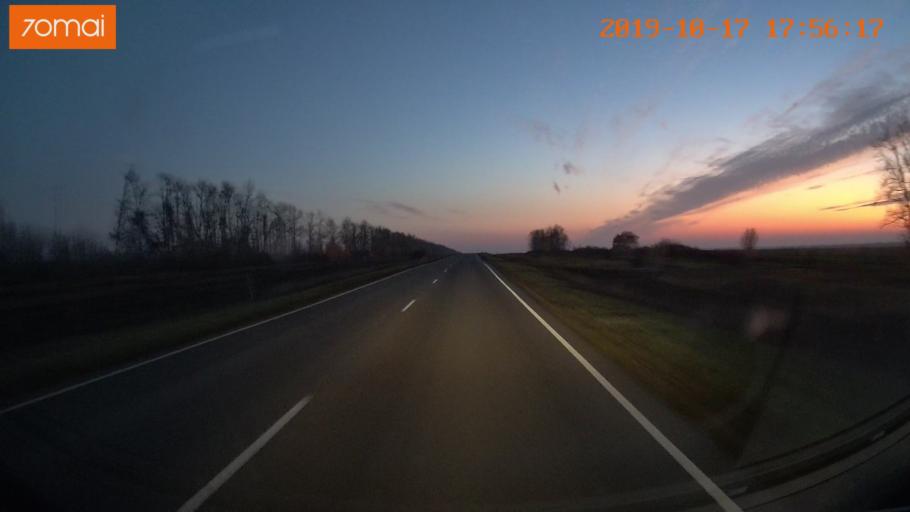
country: RU
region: Tula
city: Kurkino
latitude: 53.5815
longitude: 38.6484
